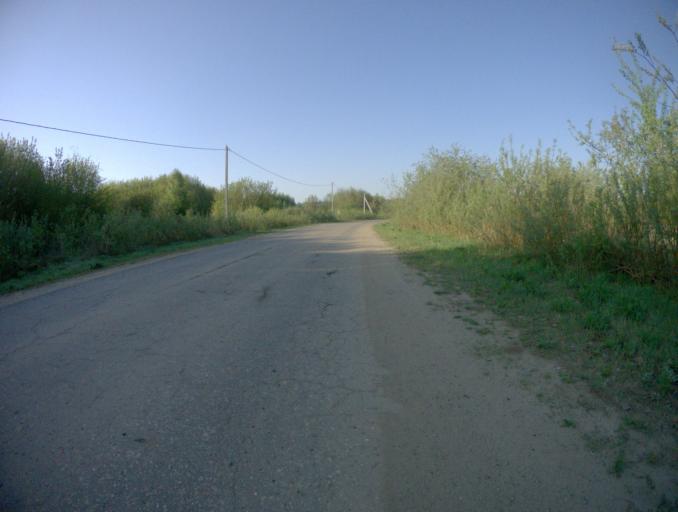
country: RU
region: Vladimir
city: Vyazniki
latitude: 56.2529
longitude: 42.1790
